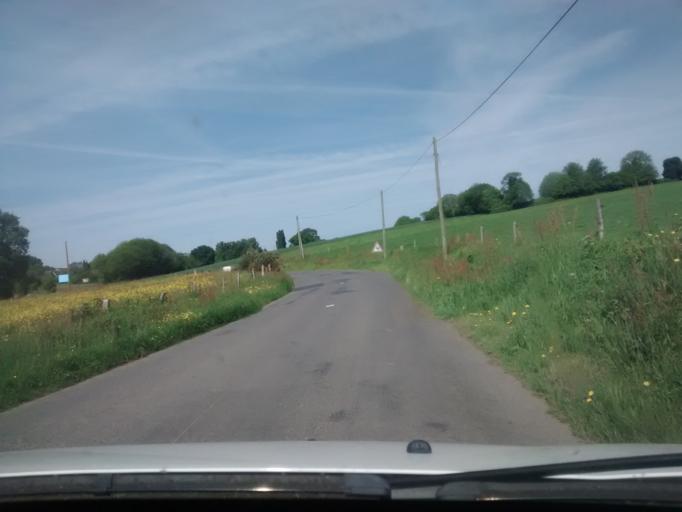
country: FR
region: Brittany
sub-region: Departement d'Ille-et-Vilaine
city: Javene
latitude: 48.3363
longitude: -1.2409
